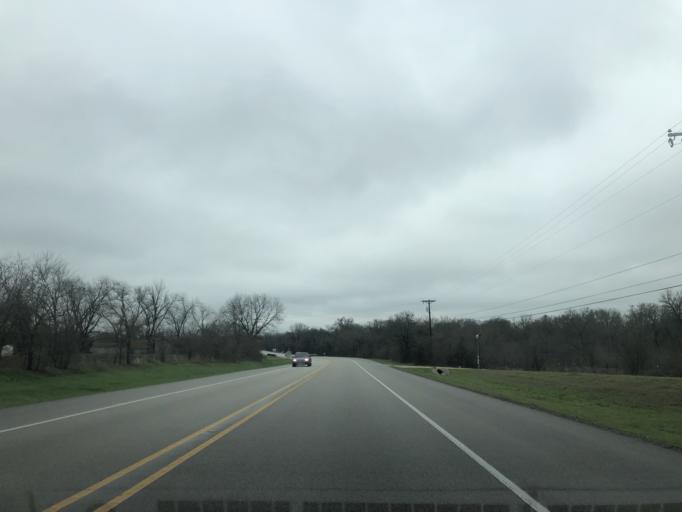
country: US
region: Texas
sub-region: Williamson County
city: Georgetown
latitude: 30.6444
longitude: -97.5782
